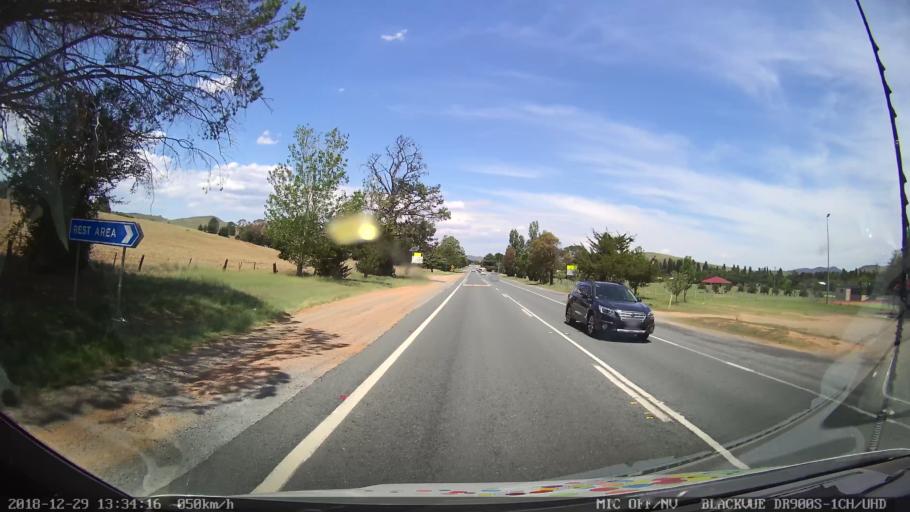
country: AU
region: New South Wales
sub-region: Cooma-Monaro
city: Cooma
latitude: -35.9519
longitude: 149.1458
